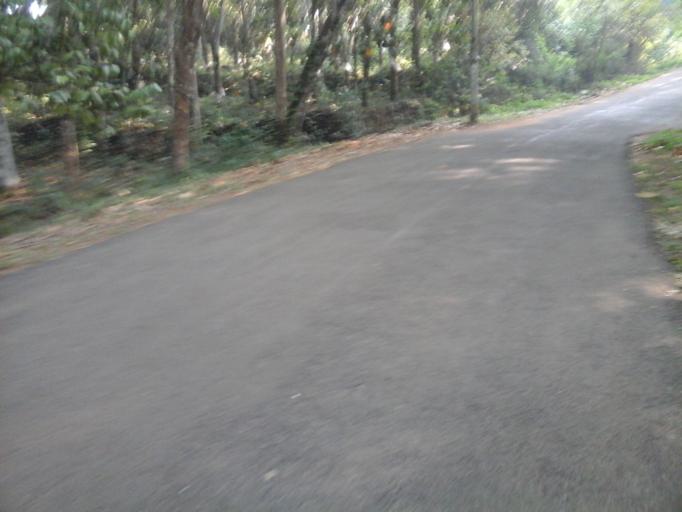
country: IN
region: Kerala
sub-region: Kottayam
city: Erattupetta
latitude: 9.5941
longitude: 76.7277
